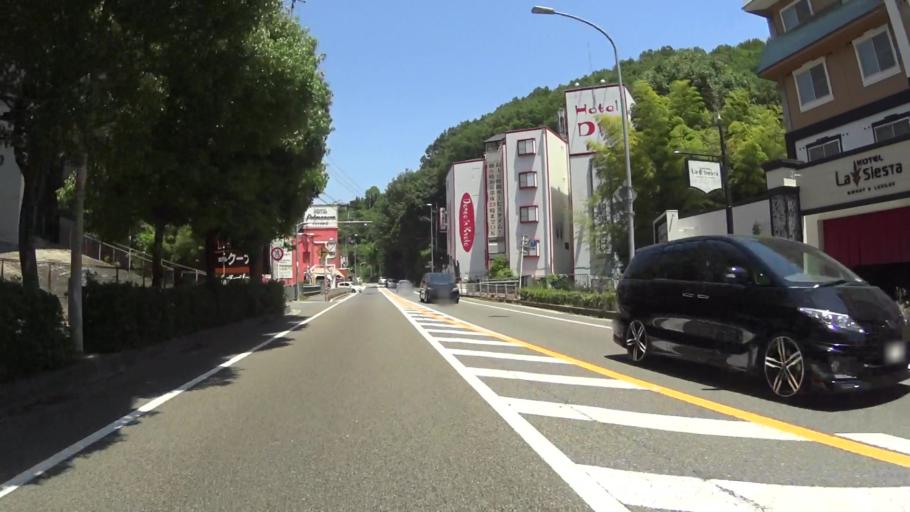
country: JP
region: Kyoto
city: Muko
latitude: 34.9809
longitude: 135.6559
